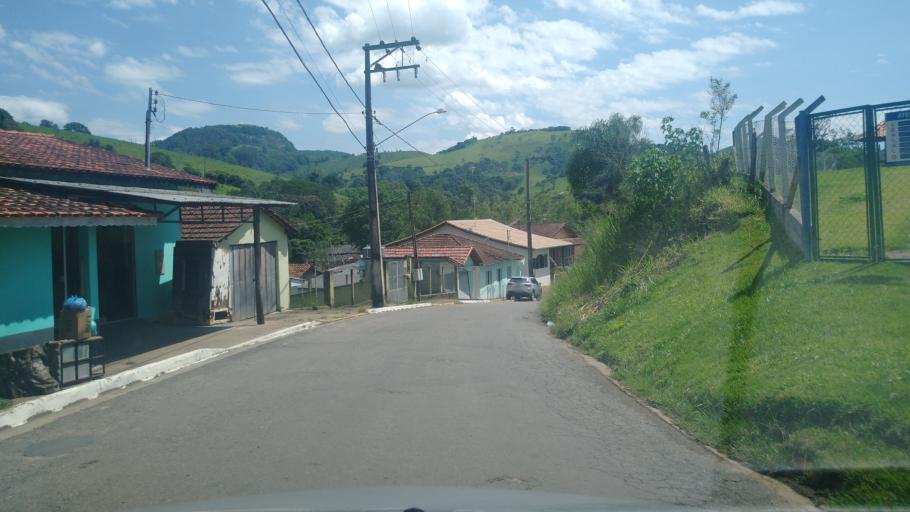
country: BR
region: Minas Gerais
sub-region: Extrema
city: Extrema
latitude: -22.7707
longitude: -46.2858
